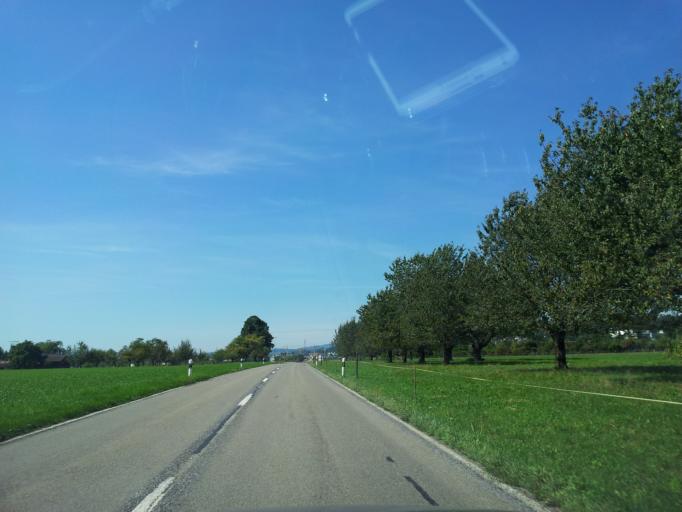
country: CH
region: Schwyz
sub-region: Bezirk March
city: Lachen
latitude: 47.2205
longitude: 8.8701
